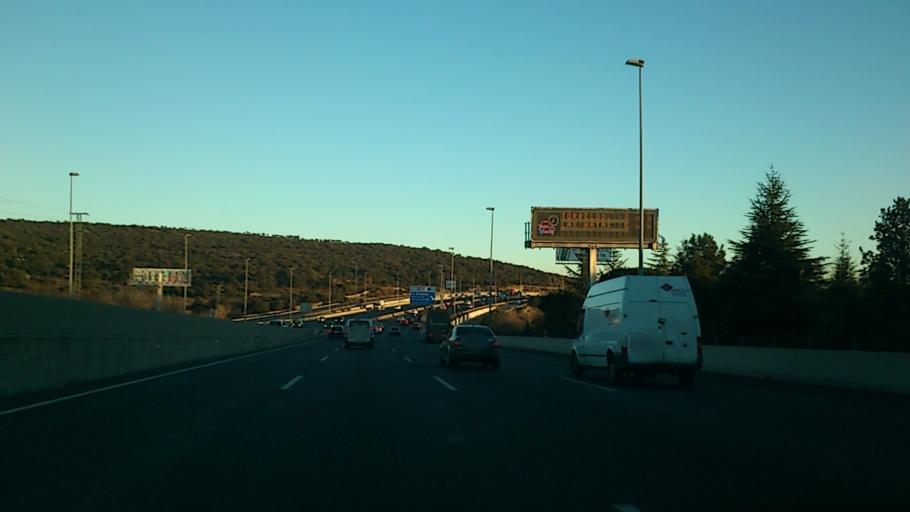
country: ES
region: Madrid
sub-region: Provincia de Madrid
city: Galapagar
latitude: 40.6053
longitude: -3.9692
